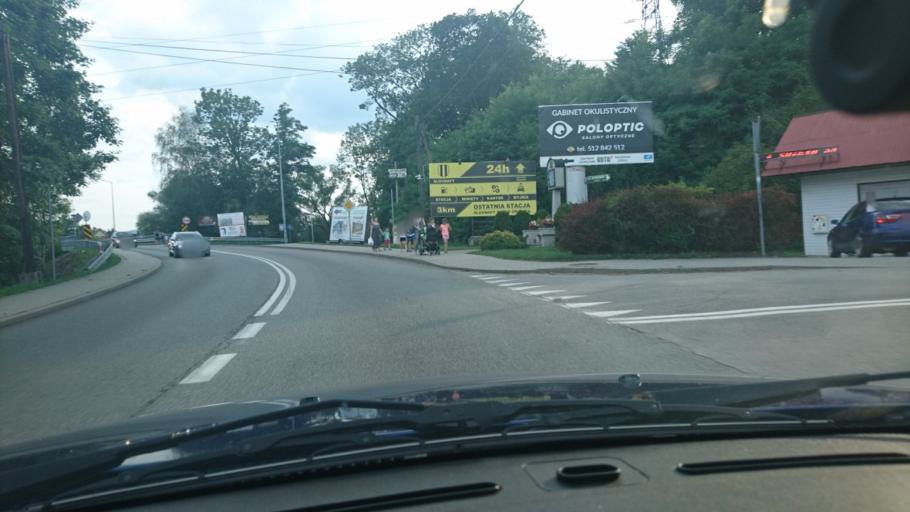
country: PL
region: Silesian Voivodeship
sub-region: Powiat zywiecki
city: Wegierska Gorka
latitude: 49.6102
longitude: 19.1165
